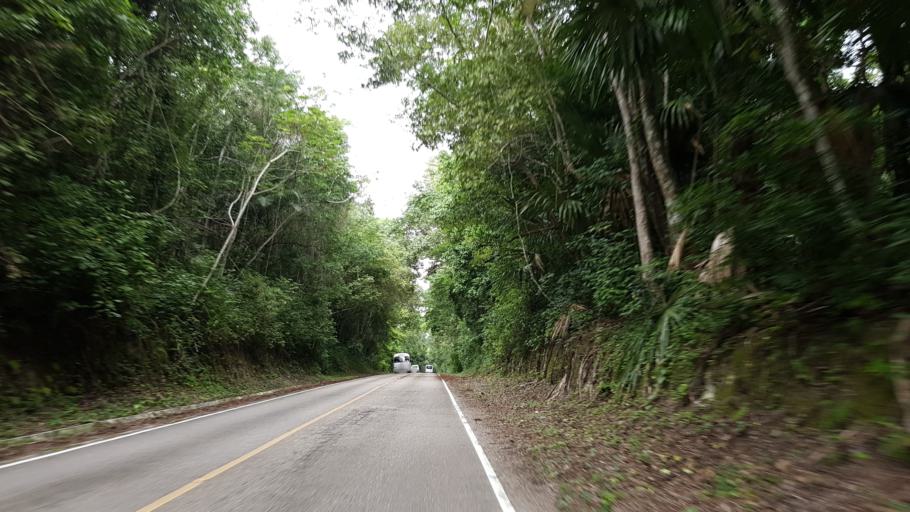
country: GT
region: Peten
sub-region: Municipio de San Jose
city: San Jose
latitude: 17.2106
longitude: -89.6155
